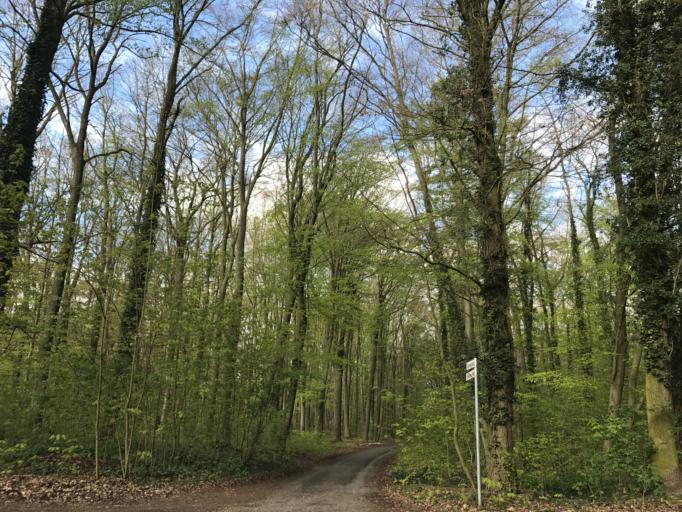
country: DE
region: Berlin
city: Kladow
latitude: 52.4758
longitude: 13.1101
